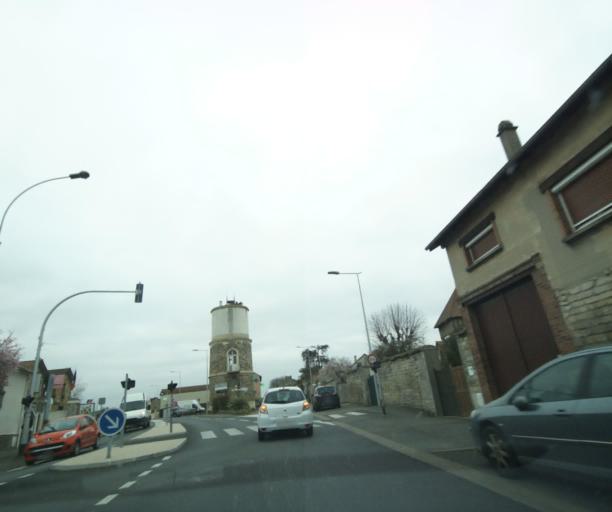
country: FR
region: Ile-de-France
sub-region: Departement des Yvelines
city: Carrieres-sous-Poissy
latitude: 48.9438
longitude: 2.0352
